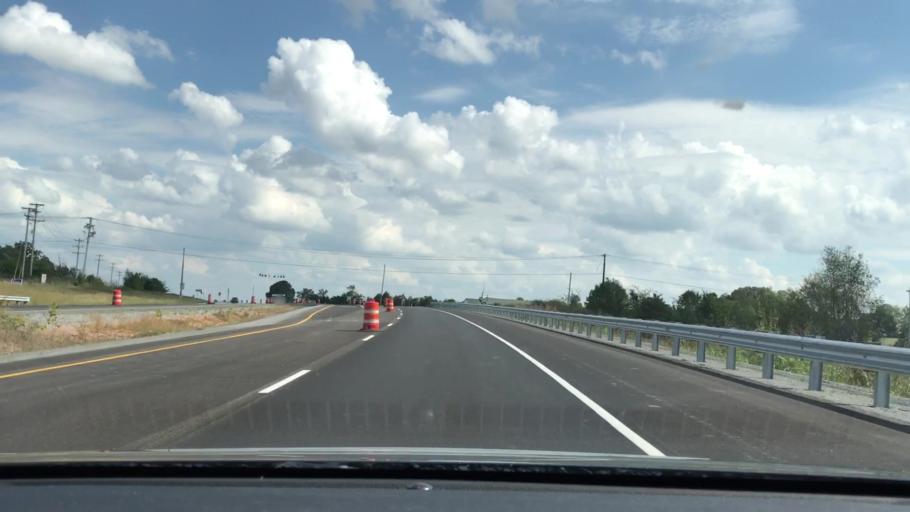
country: US
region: Kentucky
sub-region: Trigg County
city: Cadiz
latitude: 36.8429
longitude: -87.8270
